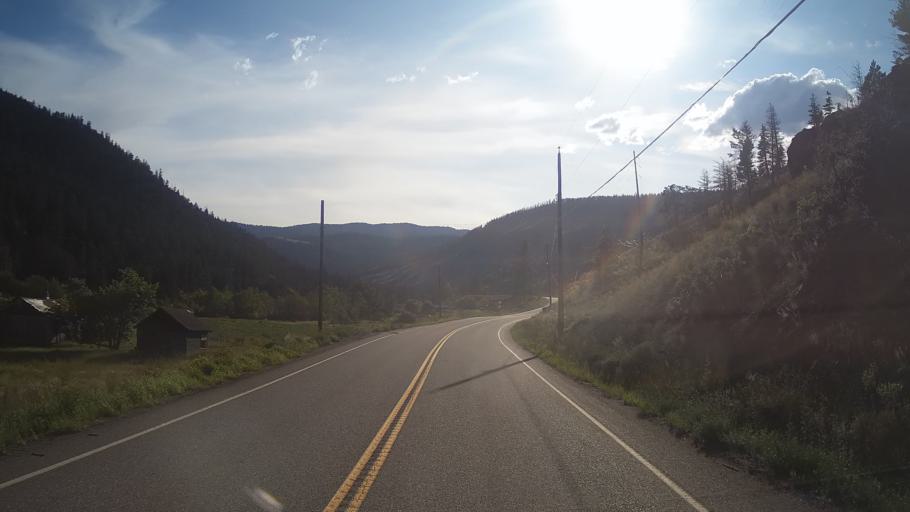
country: CA
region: British Columbia
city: Cache Creek
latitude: 50.8849
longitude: -121.4847
